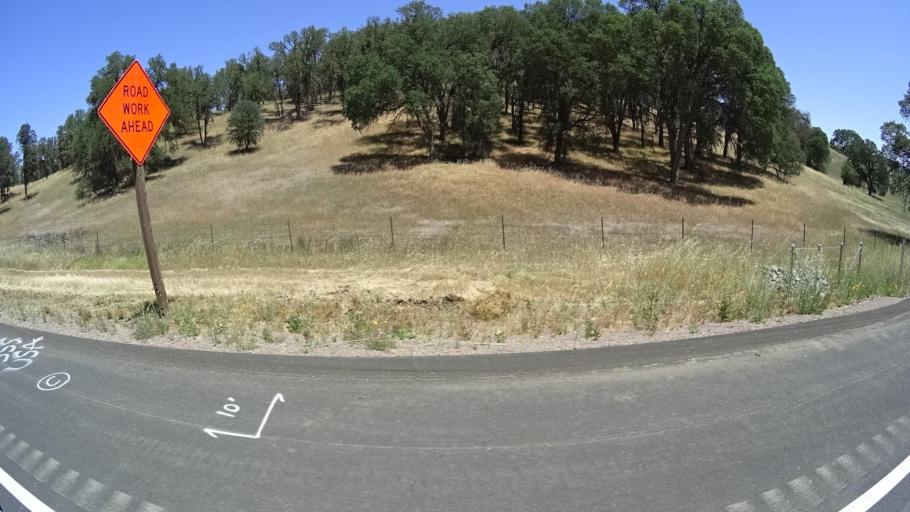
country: US
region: California
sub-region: Lake County
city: Lower Lake
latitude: 38.8988
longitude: -122.6098
